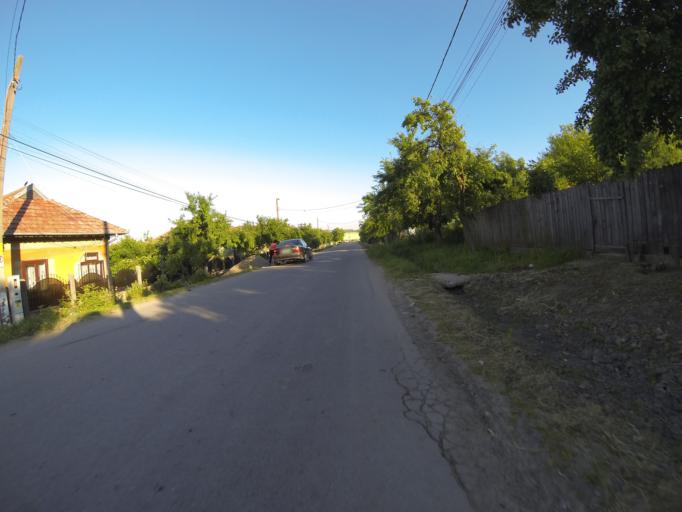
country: RO
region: Dolj
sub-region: Comuna Tuglui
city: Tuglui
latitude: 44.2039
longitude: 23.7983
